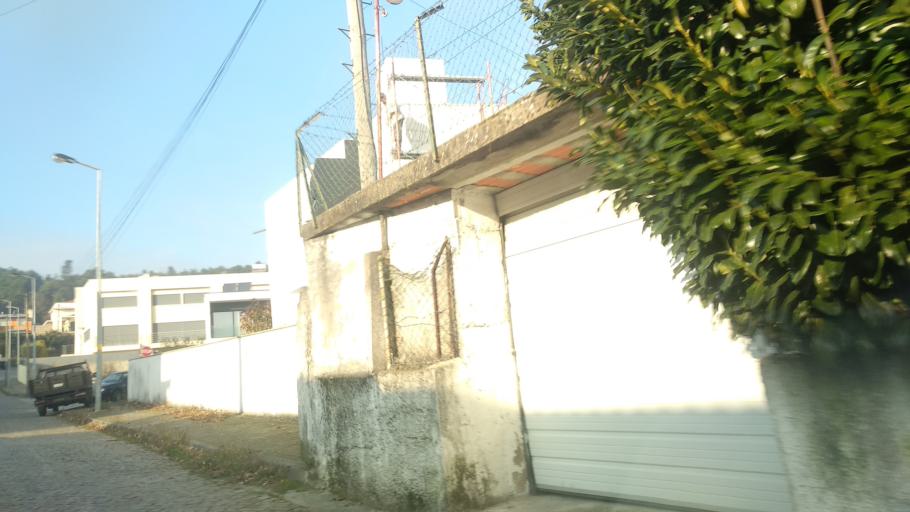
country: PT
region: Braga
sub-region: Braga
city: Adaufe
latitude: 41.5718
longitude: -8.3791
